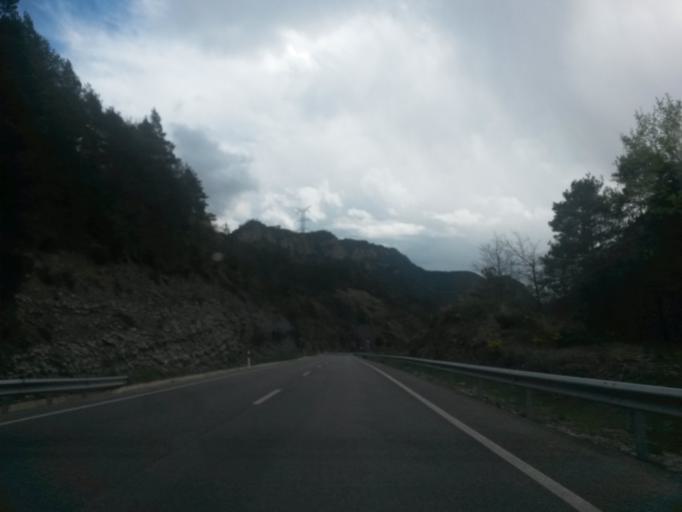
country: ES
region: Catalonia
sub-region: Provincia de Barcelona
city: Sant Julia de Cerdanyola
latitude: 42.2027
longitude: 1.8684
